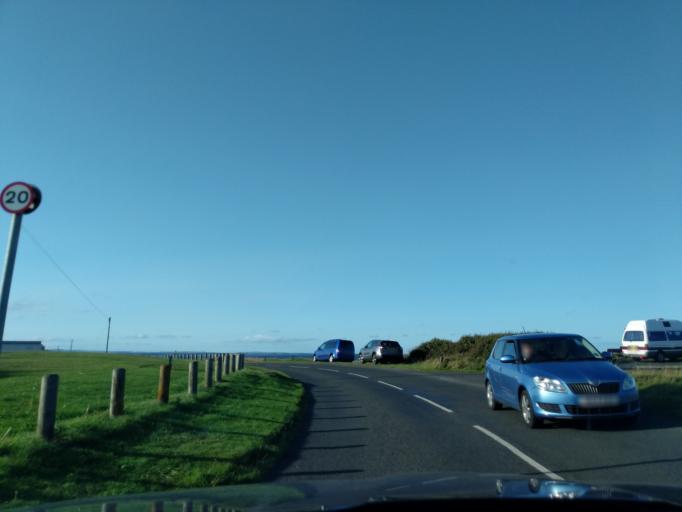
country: GB
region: England
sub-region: Northumberland
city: Lynemouth
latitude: 55.2283
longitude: -1.5291
